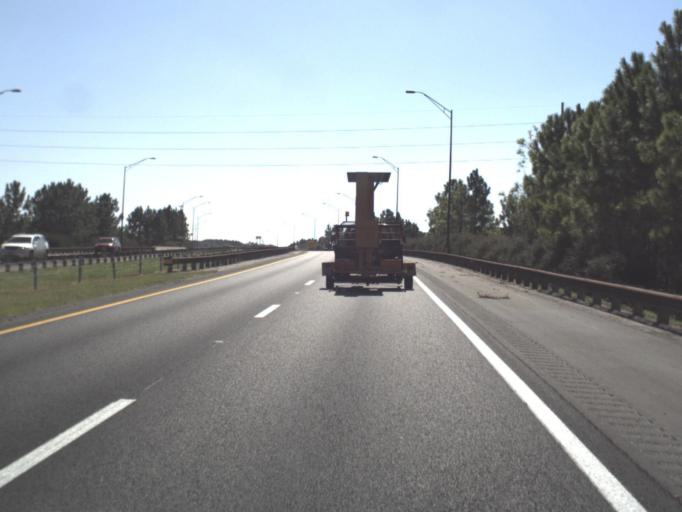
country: US
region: Florida
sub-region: Hillsborough County
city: Greater Northdale
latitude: 28.1302
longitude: -82.5487
